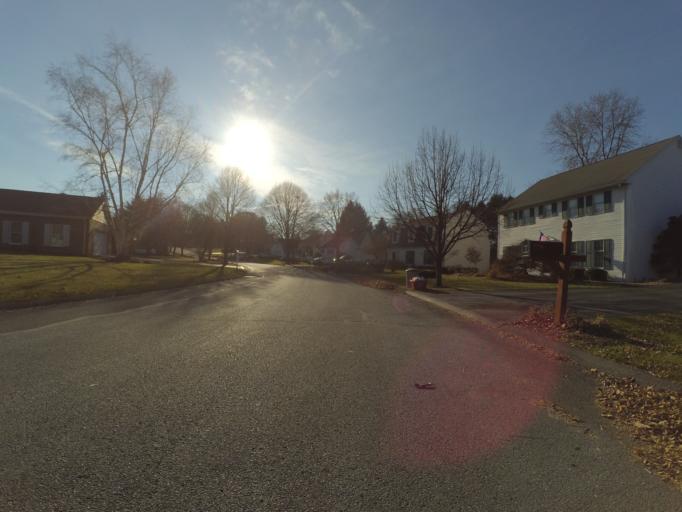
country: US
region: Pennsylvania
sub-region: Centre County
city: Lemont
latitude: 40.7994
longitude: -77.8266
